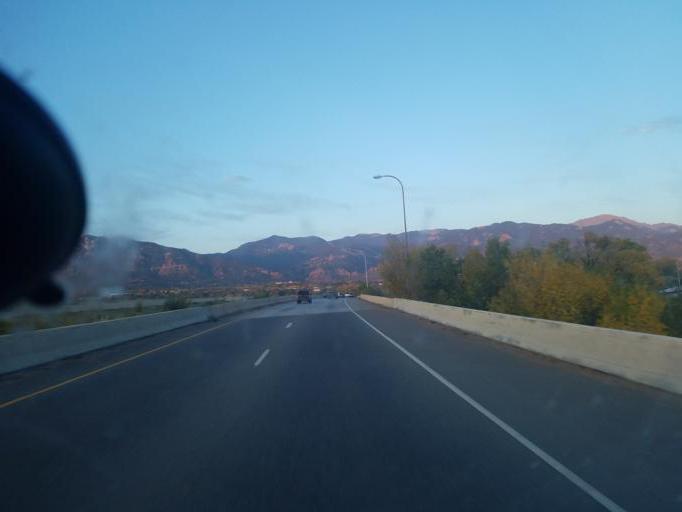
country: US
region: Colorado
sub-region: El Paso County
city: Colorado Springs
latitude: 38.8095
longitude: -104.7955
